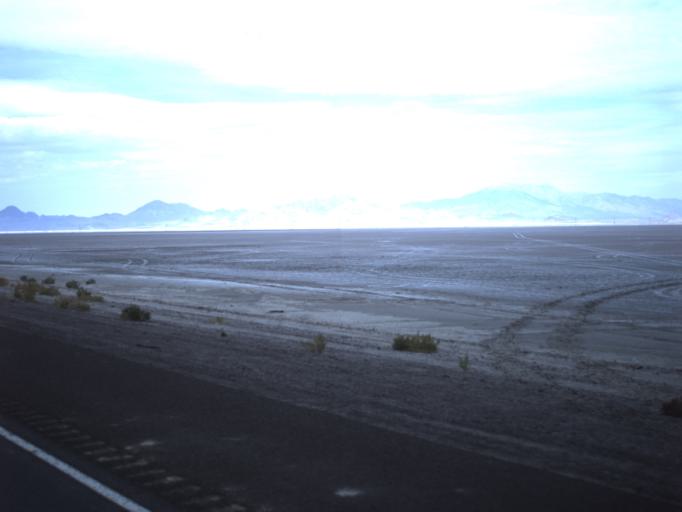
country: US
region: Utah
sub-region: Tooele County
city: Wendover
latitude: 40.7374
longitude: -113.7537
